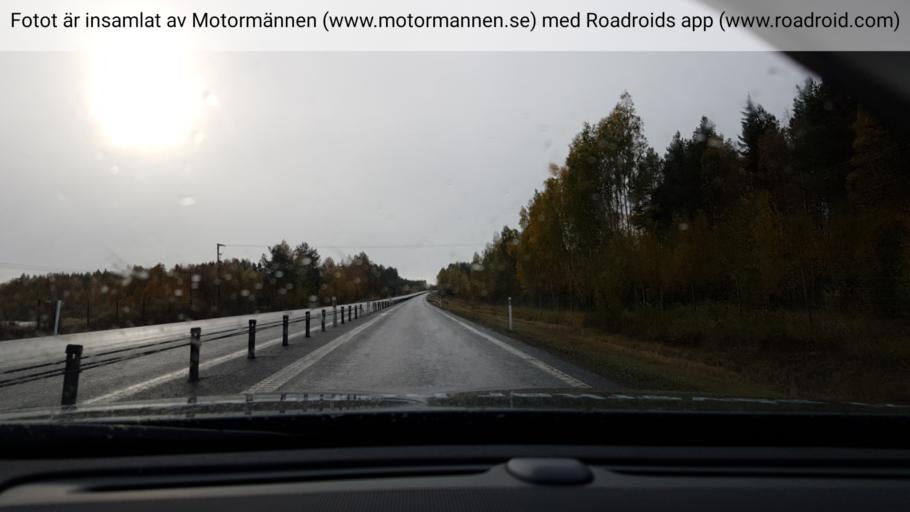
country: SE
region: Norrbotten
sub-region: Pitea Kommun
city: Pitea
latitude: 65.2852
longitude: 21.4395
